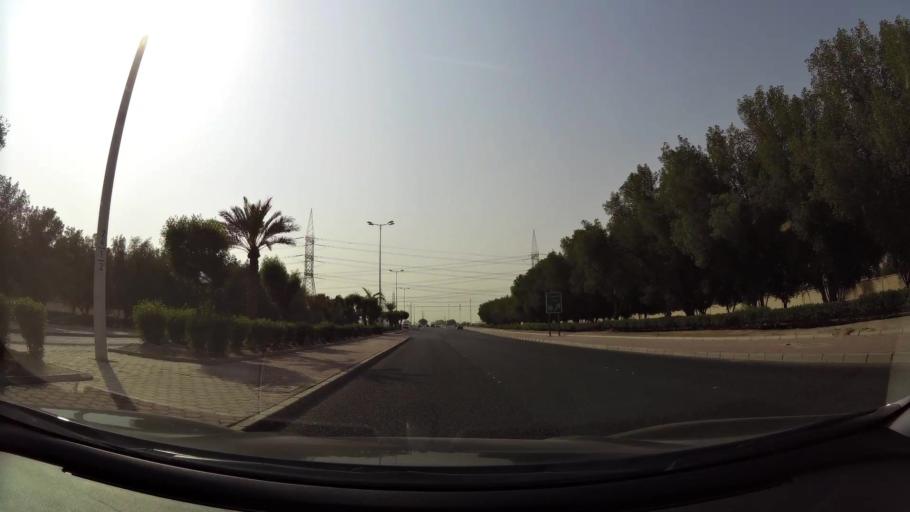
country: KW
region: Al Asimah
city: Ar Rabiyah
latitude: 29.2985
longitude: 47.8321
